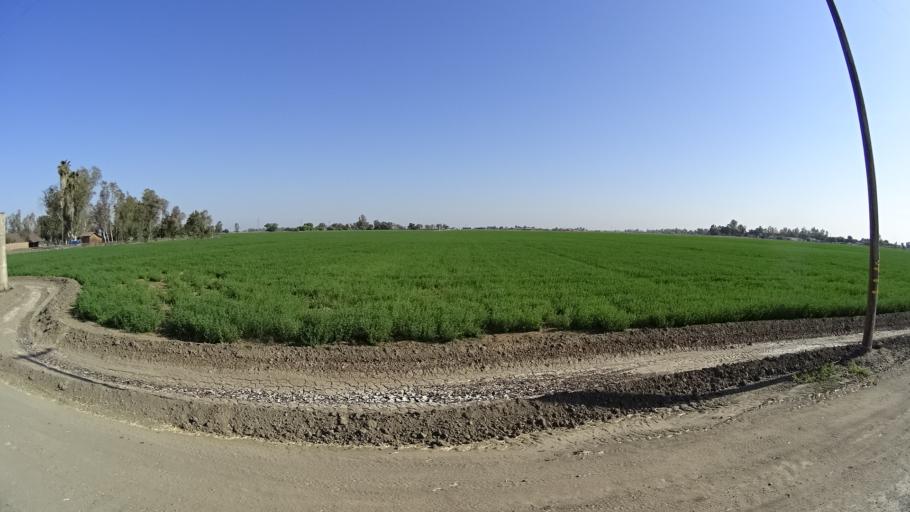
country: US
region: California
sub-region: Kings County
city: Lemoore Station
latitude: 36.3283
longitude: -119.8823
